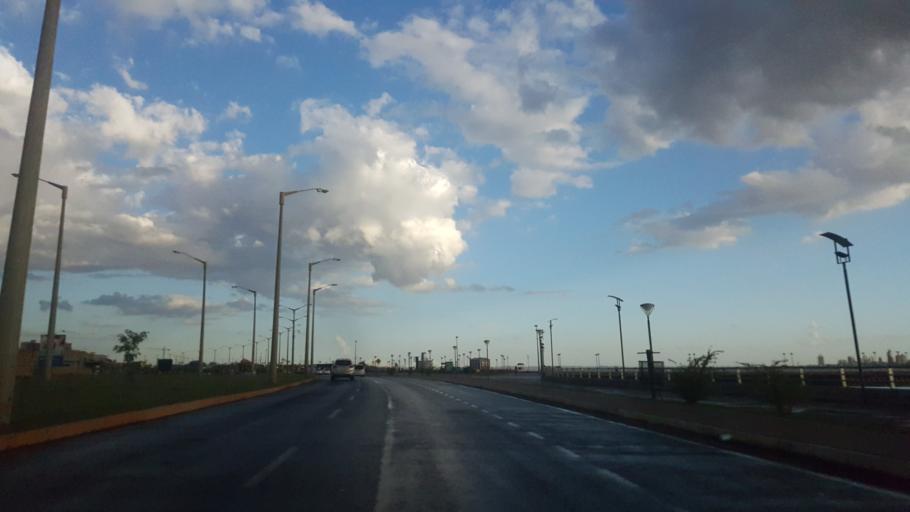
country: PY
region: Itapua
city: Encarnacion
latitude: -27.3326
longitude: -55.8751
